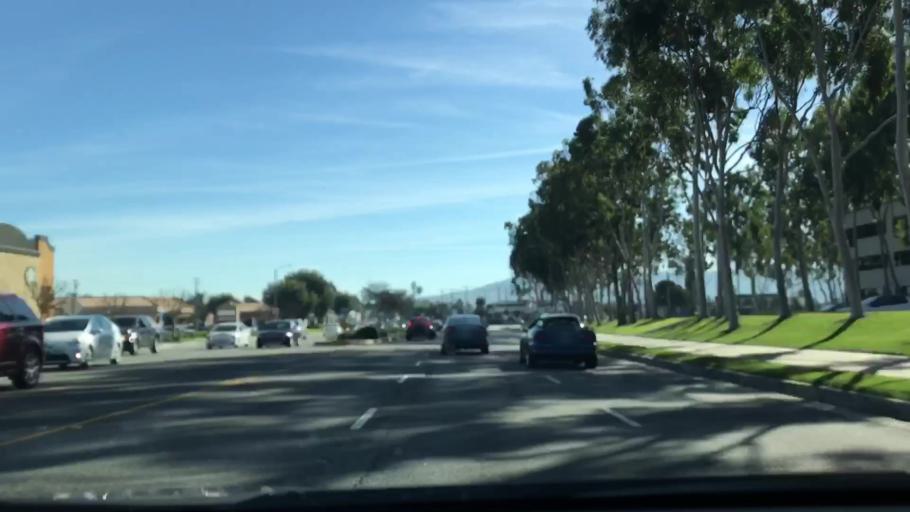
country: US
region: California
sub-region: Los Angeles County
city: Torrance
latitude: 33.8241
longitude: -118.3286
